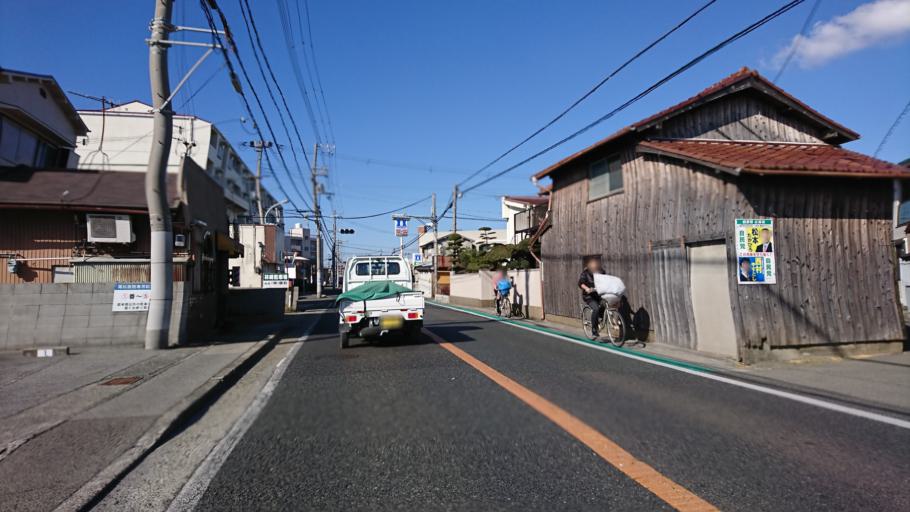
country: JP
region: Hyogo
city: Akashi
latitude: 34.6513
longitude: 134.9651
